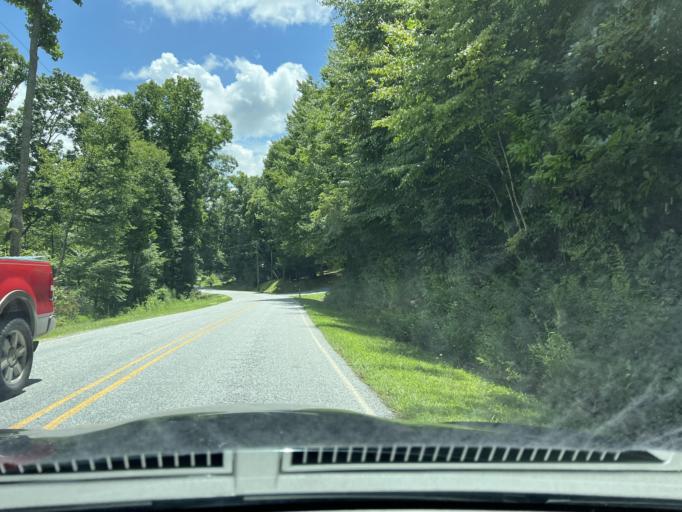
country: US
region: North Carolina
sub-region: Henderson County
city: Fruitland
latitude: 35.4161
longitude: -82.4013
